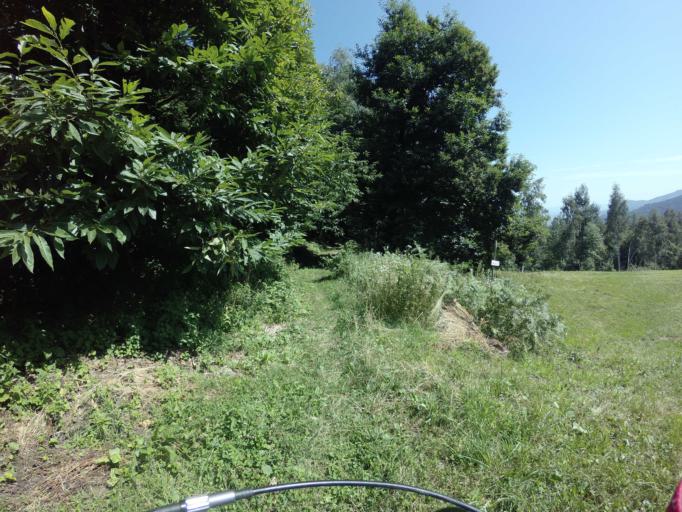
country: IT
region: Piedmont
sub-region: Provincia di Cuneo
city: Chiusa di Pesio
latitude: 44.2849
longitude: 7.6827
